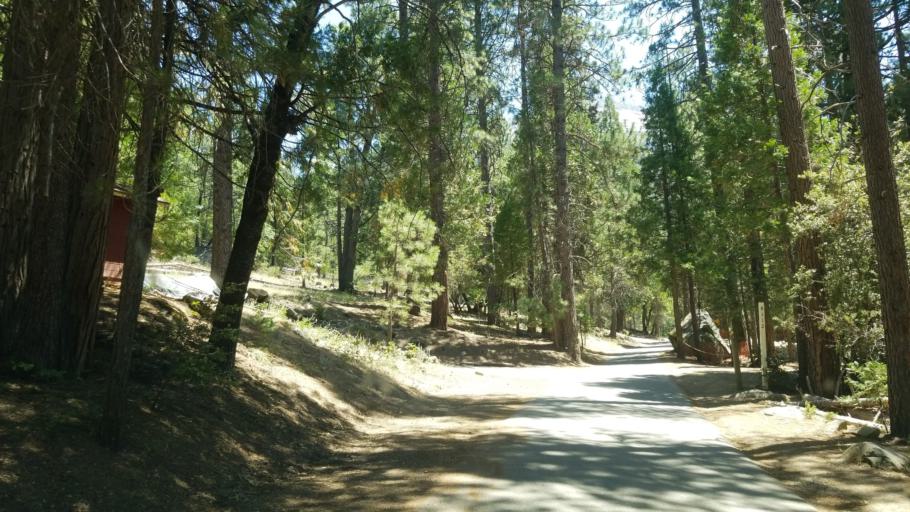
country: US
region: California
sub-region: Mariposa County
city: Yosemite Valley
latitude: 37.5483
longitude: -119.6347
